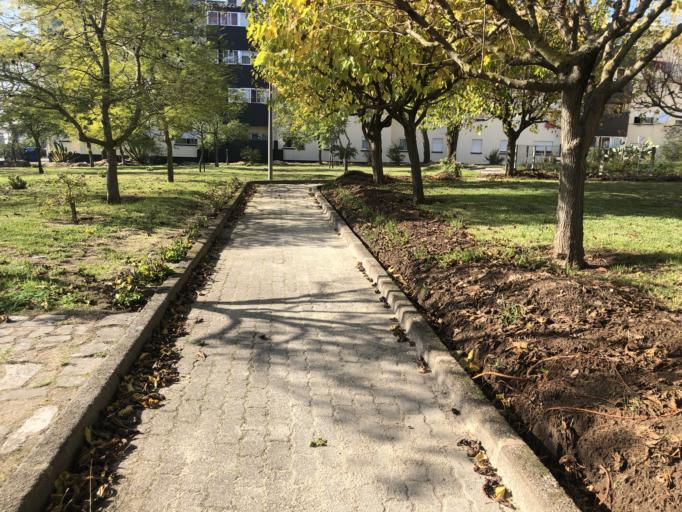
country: PT
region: Aveiro
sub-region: Estarreja
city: Estarreja
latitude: 40.7598
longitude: -8.5746
